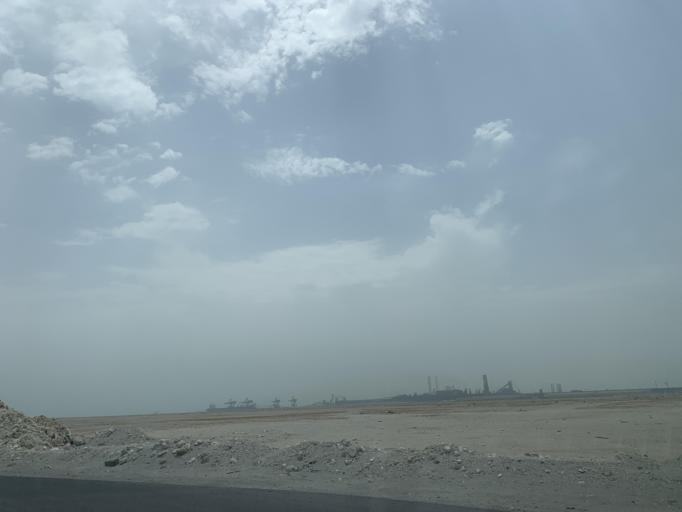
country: BH
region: Muharraq
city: Al Hadd
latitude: 26.2128
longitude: 50.7002
